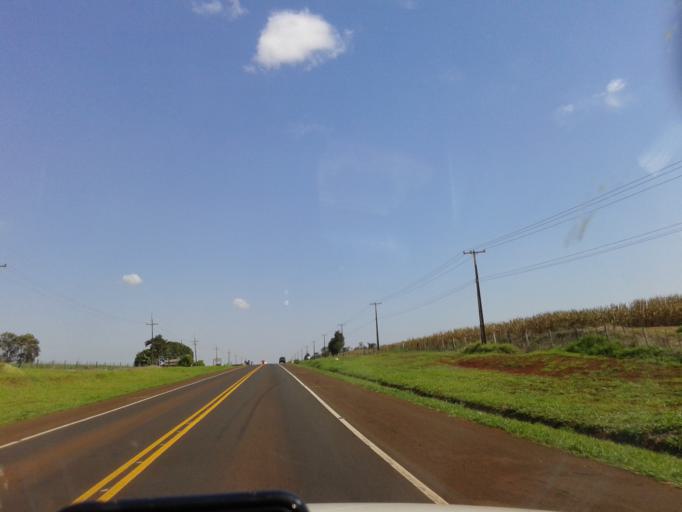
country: PY
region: Alto Parana
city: Colonia Yguazu
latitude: -25.6201
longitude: -54.9553
